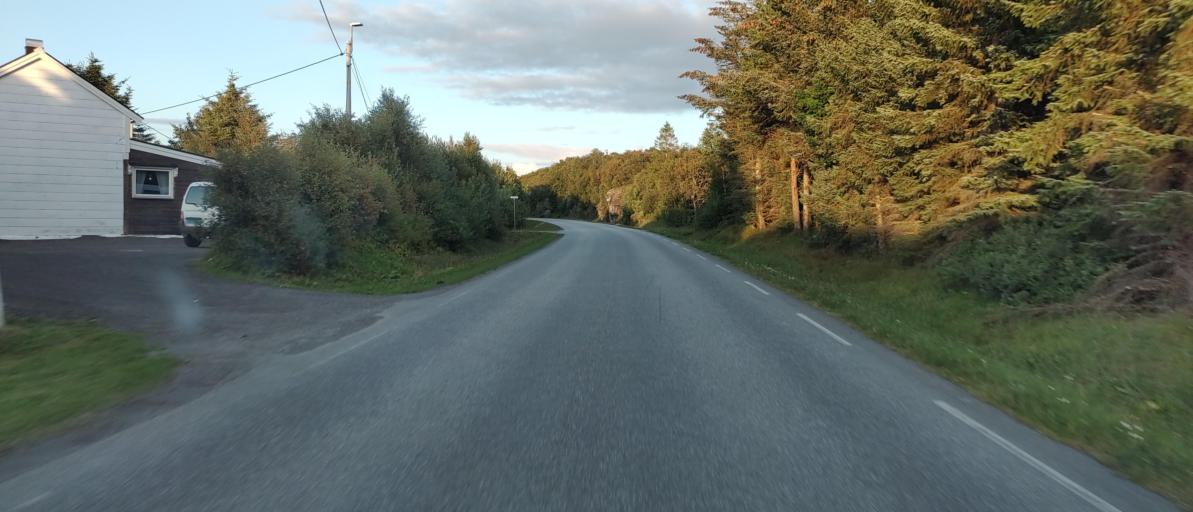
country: NO
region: More og Romsdal
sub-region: Fraena
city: Elnesvagen
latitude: 62.9908
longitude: 7.1819
